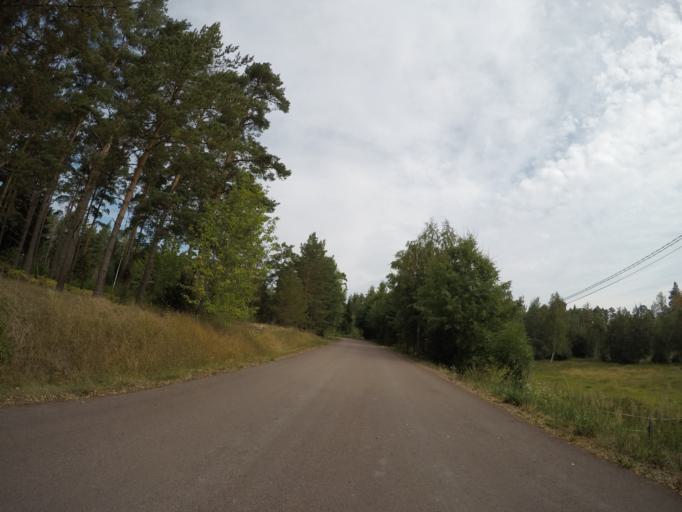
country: AX
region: Alands landsbygd
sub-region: Finstroem
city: Finstroem
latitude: 60.2539
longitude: 19.9145
